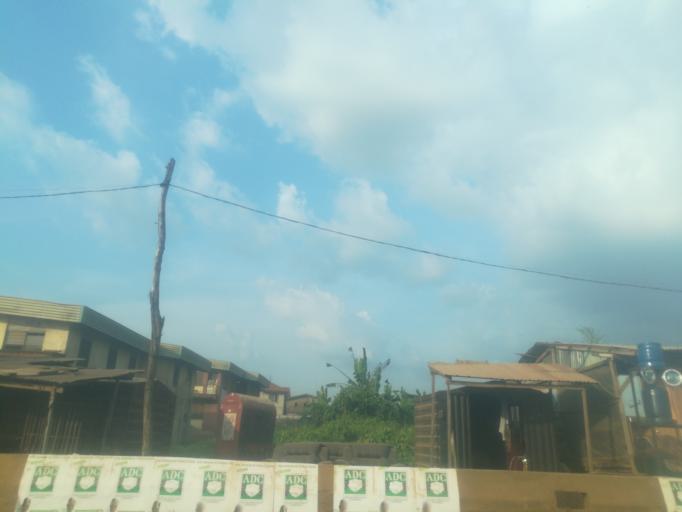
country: NG
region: Ogun
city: Abeokuta
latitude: 7.1687
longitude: 3.2977
